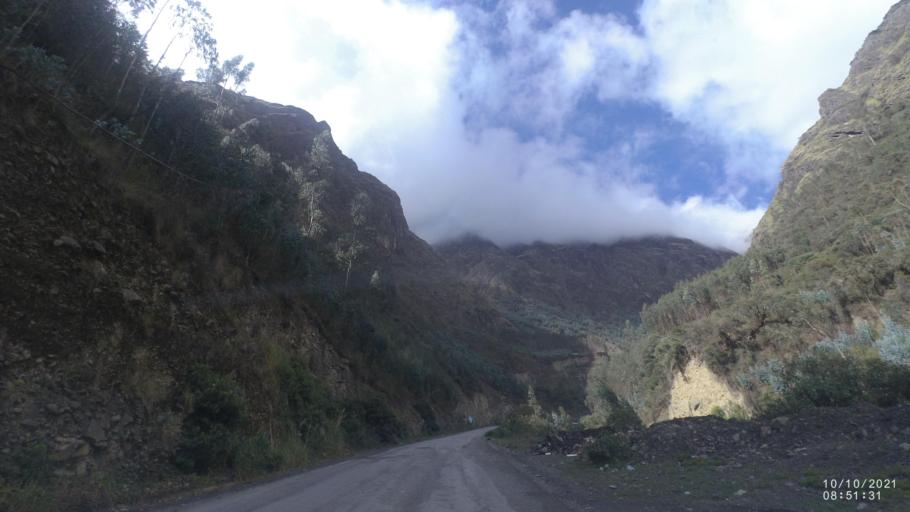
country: BO
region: La Paz
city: Quime
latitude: -16.9828
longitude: -67.2272
